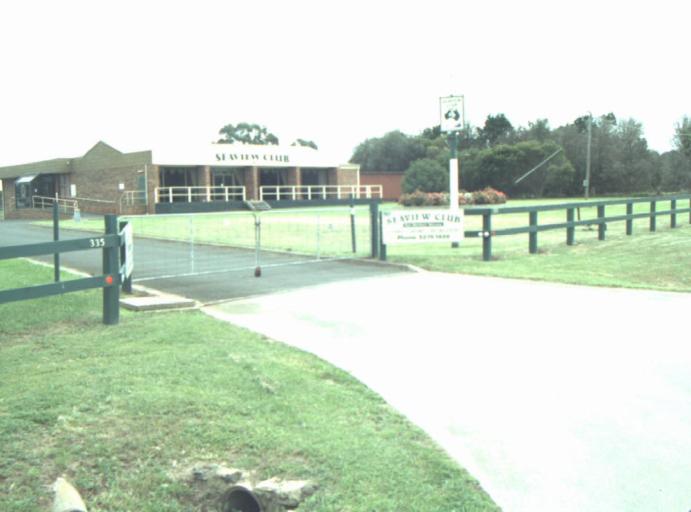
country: AU
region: Victoria
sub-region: Greater Geelong
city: Bell Post Hill
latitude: -38.0752
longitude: 144.3278
